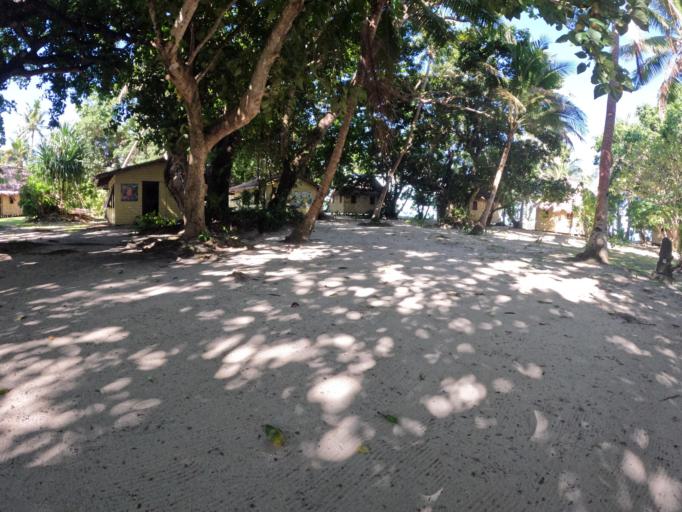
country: FJ
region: Central
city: Suva
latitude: -17.8094
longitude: 178.7224
